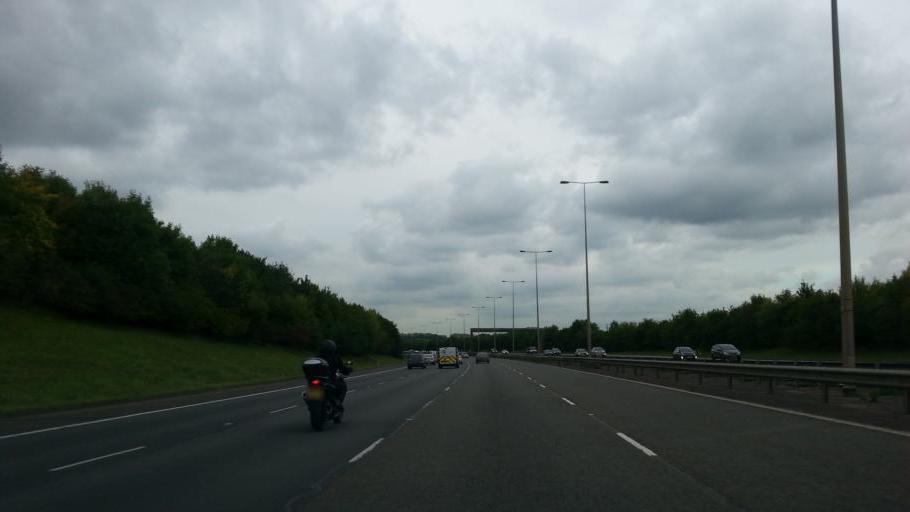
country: GB
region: England
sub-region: Cambridgeshire
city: Stilton
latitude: 52.4852
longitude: -0.2855
